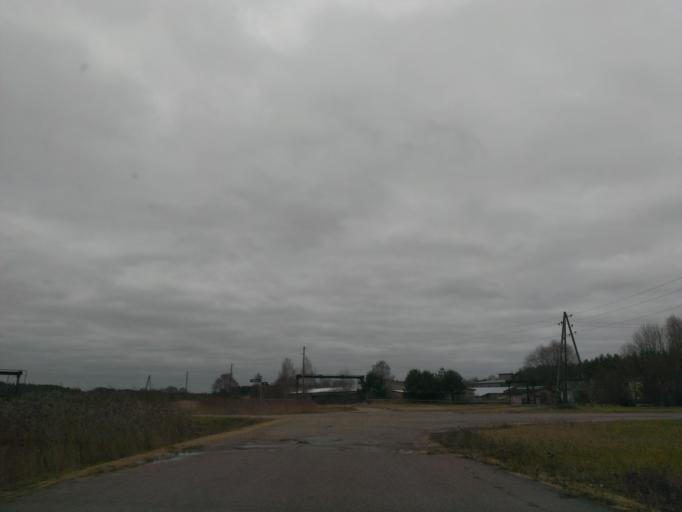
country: LV
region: Adazi
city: Adazi
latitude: 57.0630
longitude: 24.3343
